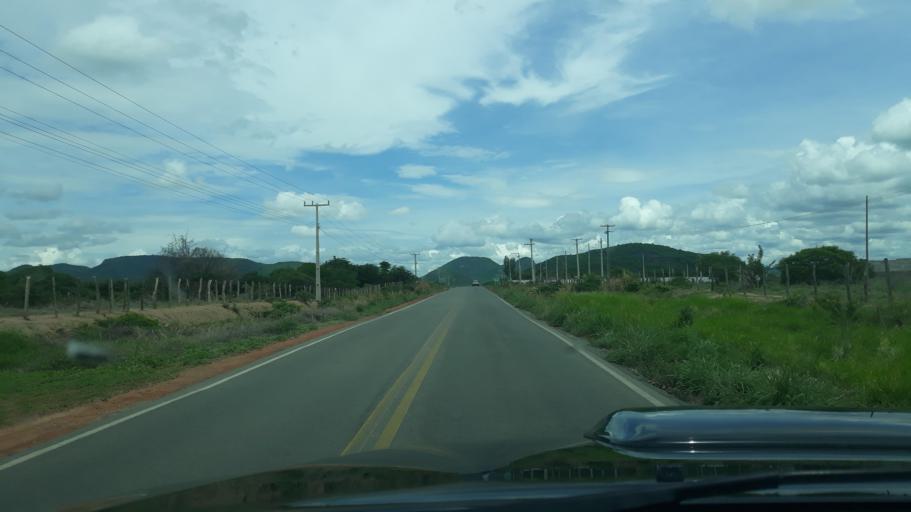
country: BR
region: Bahia
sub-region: Guanambi
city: Guanambi
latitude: -14.2486
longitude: -42.7513
